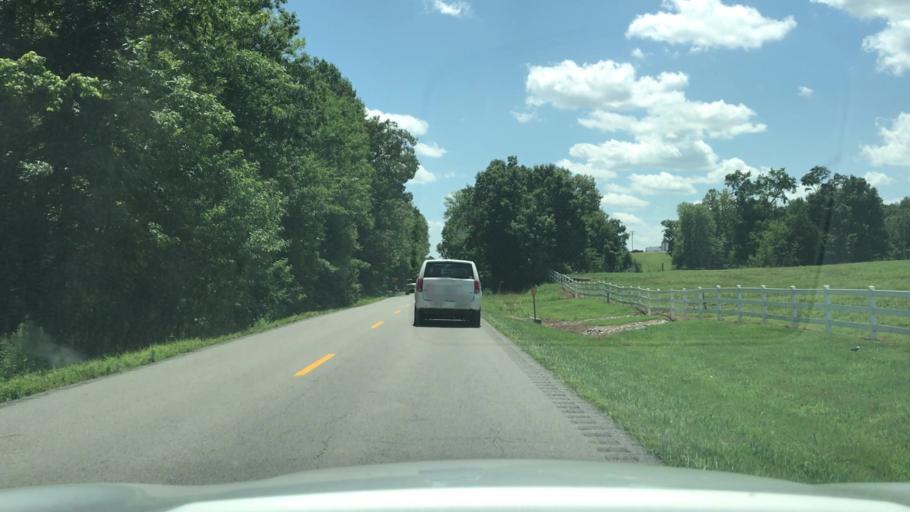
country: US
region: Kentucky
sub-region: Christian County
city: Hopkinsville
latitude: 36.9085
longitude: -87.4446
